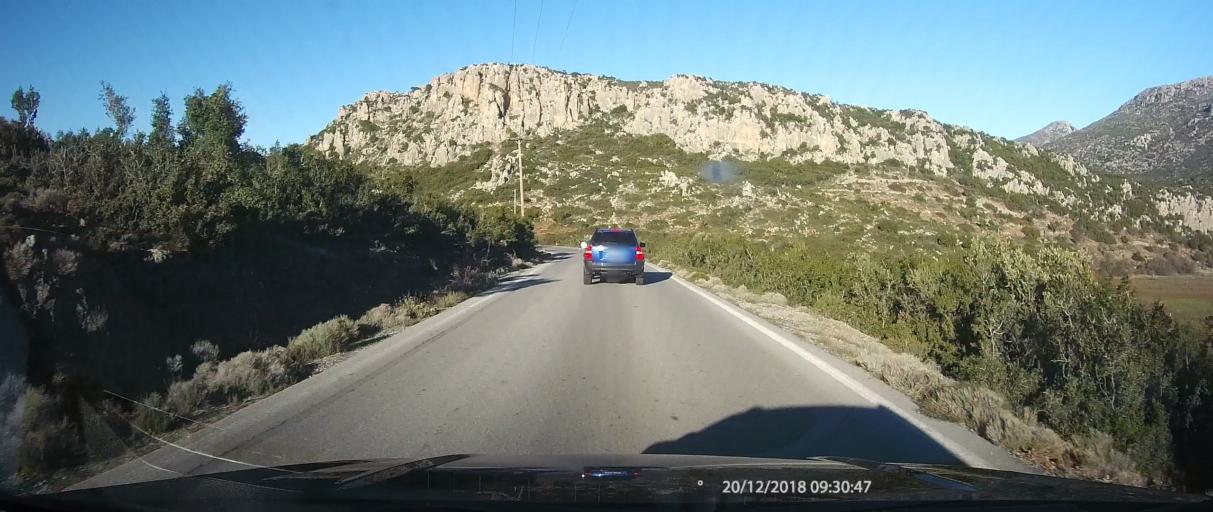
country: GR
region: Peloponnese
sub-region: Nomos Lakonias
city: Kato Glikovrisi
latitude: 36.9525
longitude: 22.8418
